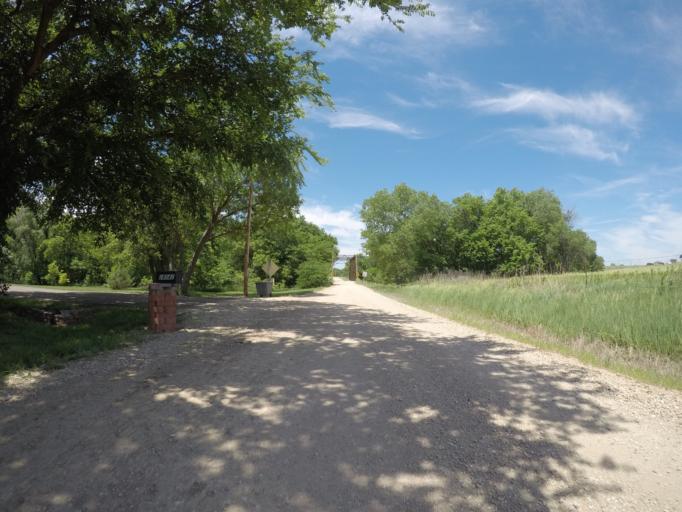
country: US
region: Kansas
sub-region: Wabaunsee County
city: Alma
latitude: 39.0290
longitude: -96.2799
